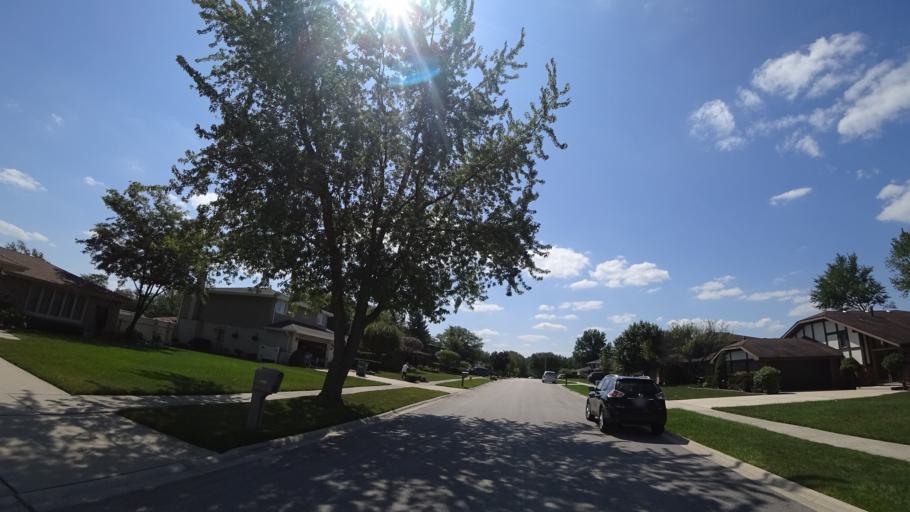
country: US
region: Illinois
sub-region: Cook County
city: Orland Park
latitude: 41.6335
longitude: -87.8417
